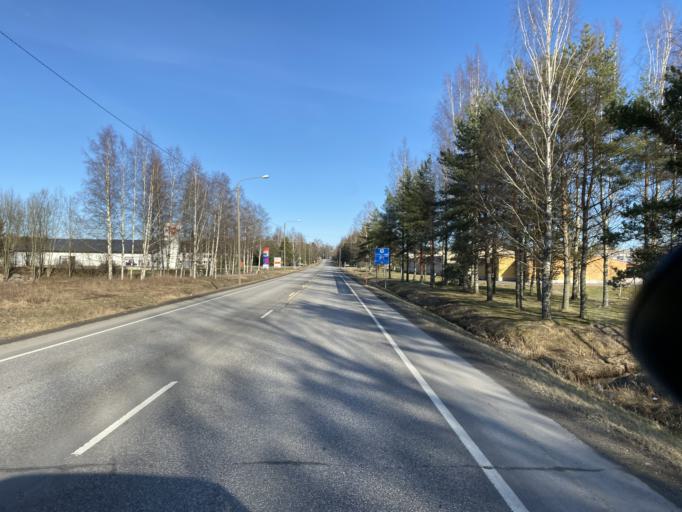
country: FI
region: Satakunta
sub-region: Rauma
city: Eura
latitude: 61.1313
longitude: 22.1396
